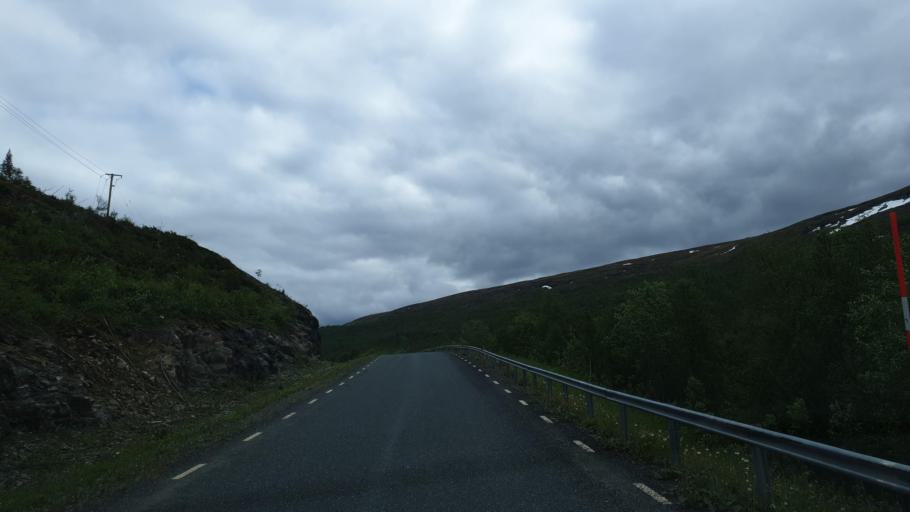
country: NO
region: Nordland
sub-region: Hattfjelldal
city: Hattfjelldal
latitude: 65.4241
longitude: 14.6050
